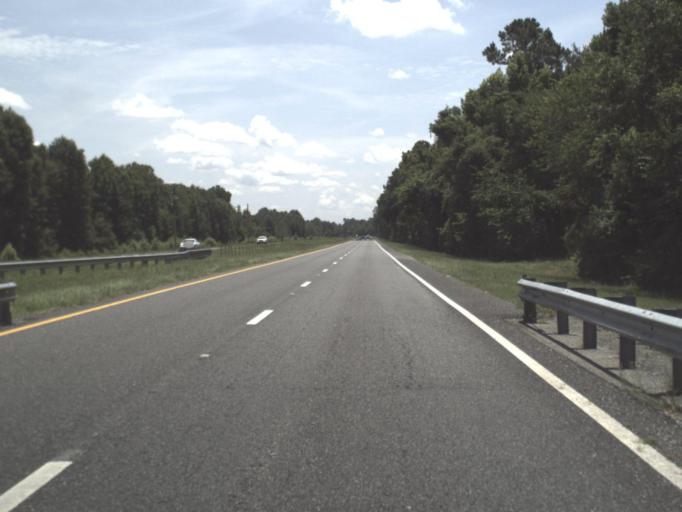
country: US
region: Florida
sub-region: Taylor County
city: Steinhatchee
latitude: 29.6893
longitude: -83.2710
